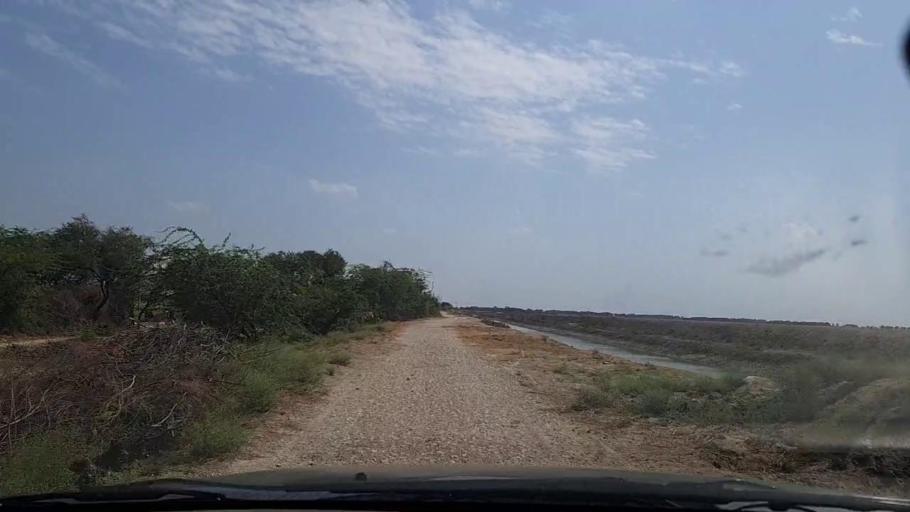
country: PK
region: Sindh
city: Mirpur Batoro
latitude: 24.5744
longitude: 68.1967
